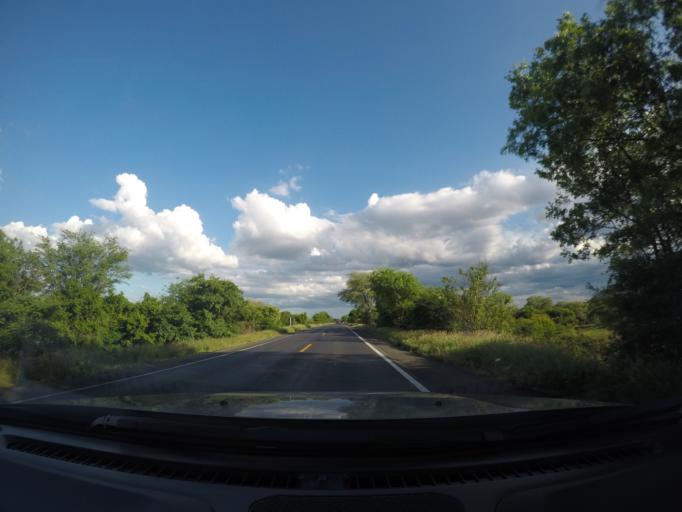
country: BR
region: Bahia
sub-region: Oliveira Dos Brejinhos
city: Beira Rio
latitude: -12.2318
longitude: -42.7800
